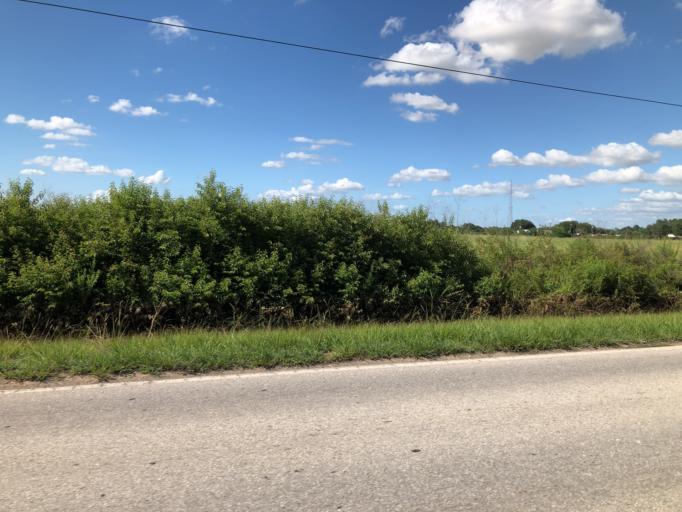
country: US
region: Texas
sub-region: Harris County
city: Katy
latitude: 29.8314
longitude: -95.8101
